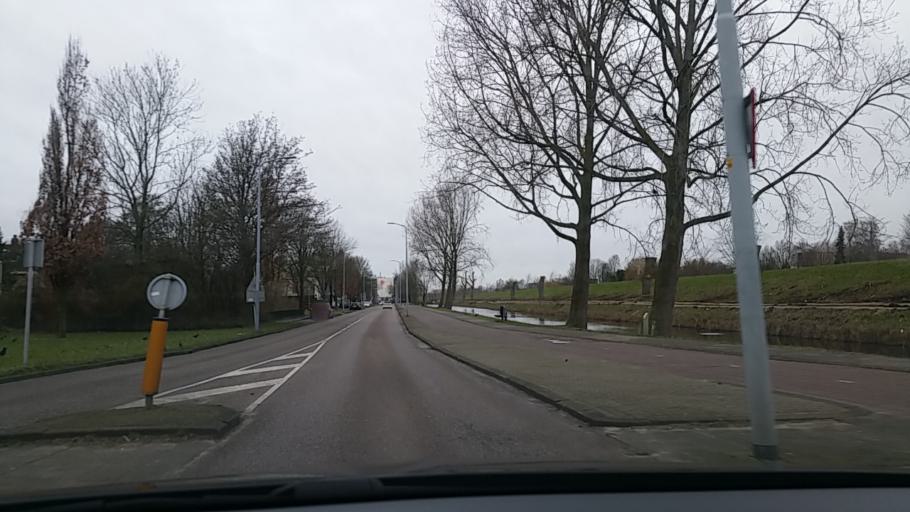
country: NL
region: North Holland
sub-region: Gemeente Haarlemmermeer
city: Hoofddorp
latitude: 52.2936
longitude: 4.6952
